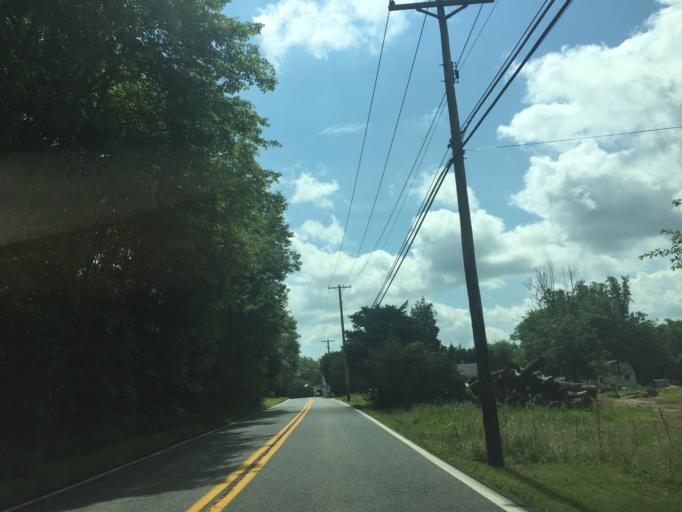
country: US
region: Maryland
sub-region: Baltimore County
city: Kingsville
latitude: 39.4386
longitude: -76.4051
